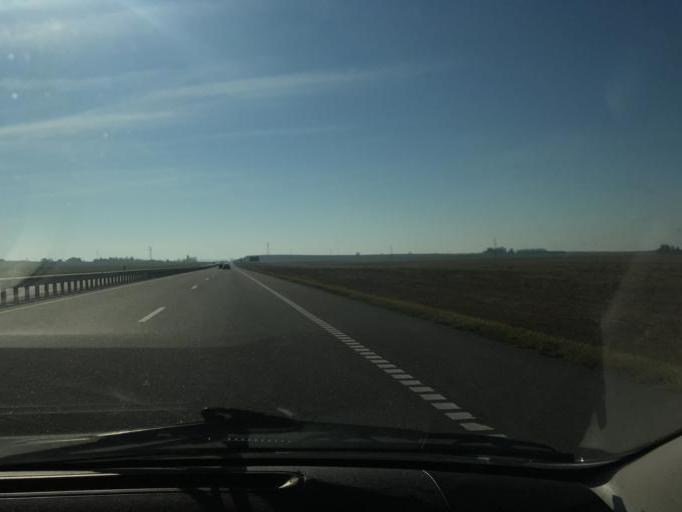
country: BY
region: Minsk
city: Slutsk
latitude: 53.1940
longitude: 27.5509
